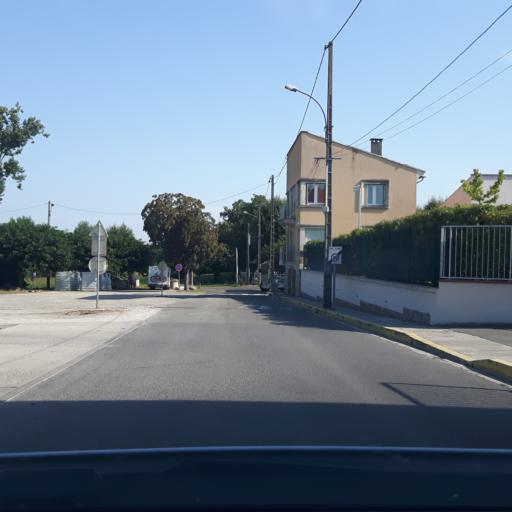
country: FR
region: Midi-Pyrenees
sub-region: Departement de la Haute-Garonne
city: Grenade
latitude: 43.7724
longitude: 1.2964
